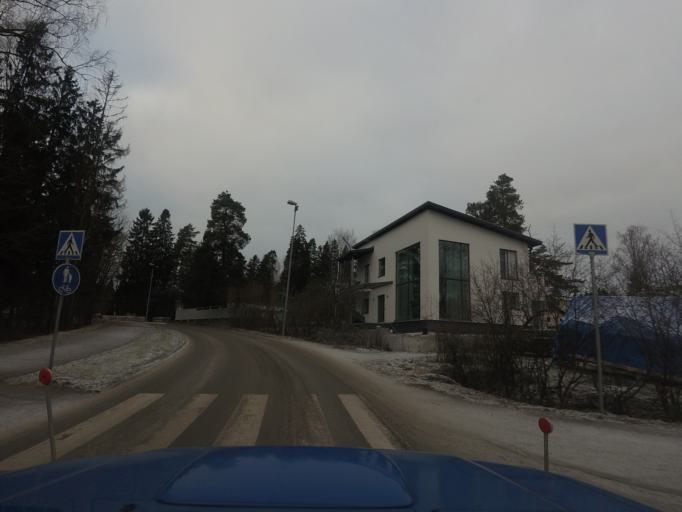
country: FI
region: Uusimaa
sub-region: Helsinki
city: Espoo
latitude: 60.2136
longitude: 24.6387
